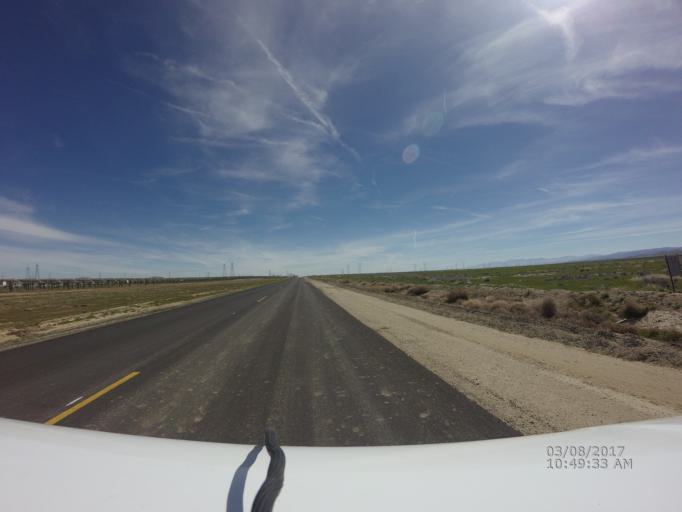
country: US
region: California
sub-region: Los Angeles County
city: Green Valley
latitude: 34.8188
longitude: -118.4223
